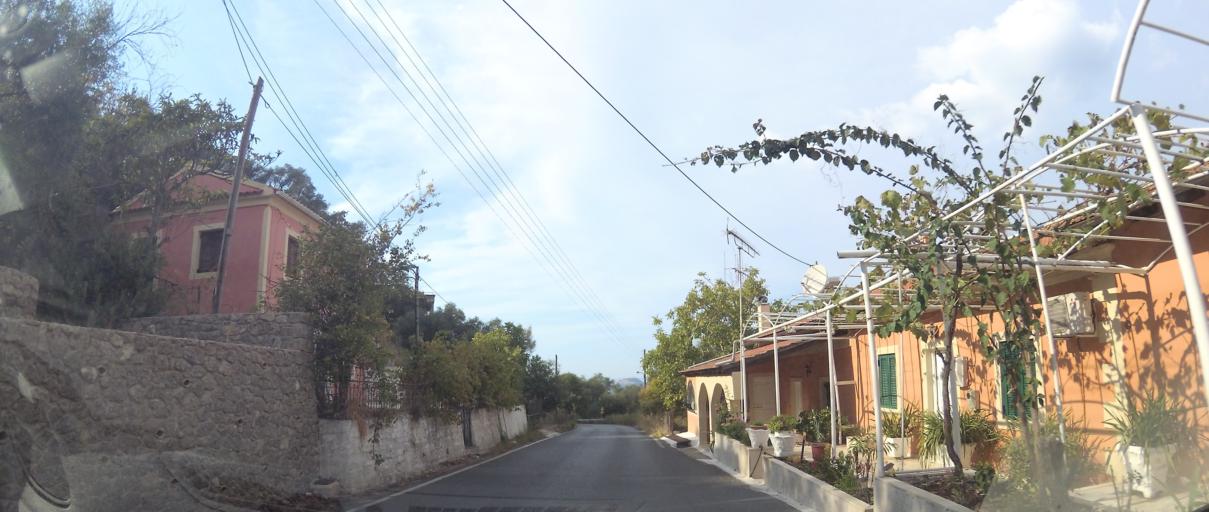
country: GR
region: Ionian Islands
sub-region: Nomos Kerkyras
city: Kynopiastes
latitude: 39.5539
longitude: 19.8613
